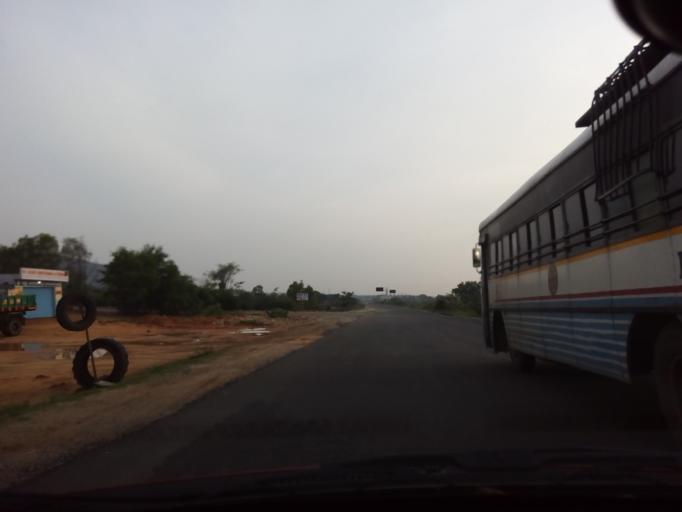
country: IN
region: Karnataka
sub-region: Chikkaballapur
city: Gudibanda
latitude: 13.6108
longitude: 77.7886
